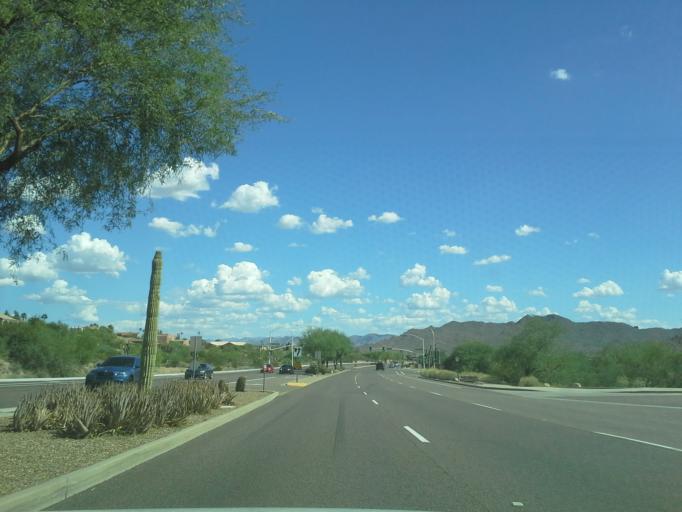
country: US
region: Arizona
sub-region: Maricopa County
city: Fountain Hills
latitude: 33.5771
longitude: -111.7219
